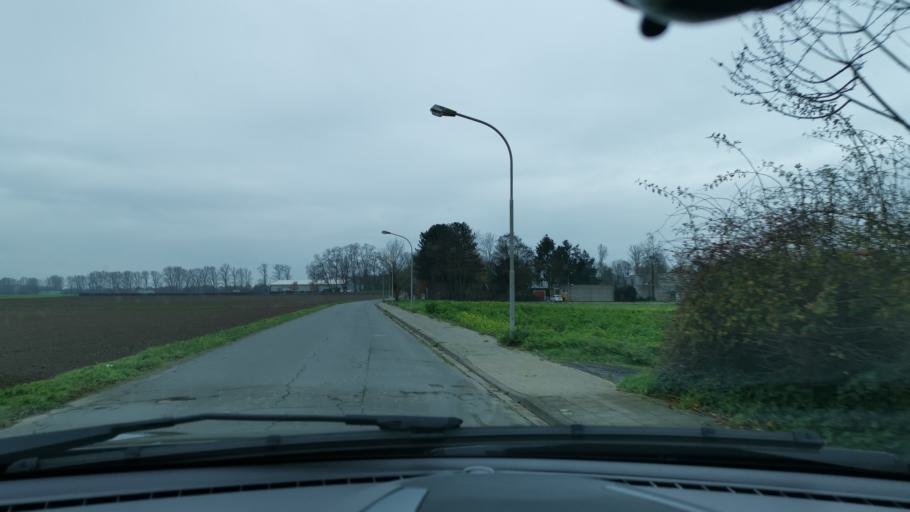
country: DE
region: North Rhine-Westphalia
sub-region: Regierungsbezirk Dusseldorf
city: Neubrueck
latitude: 51.1186
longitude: 6.6818
